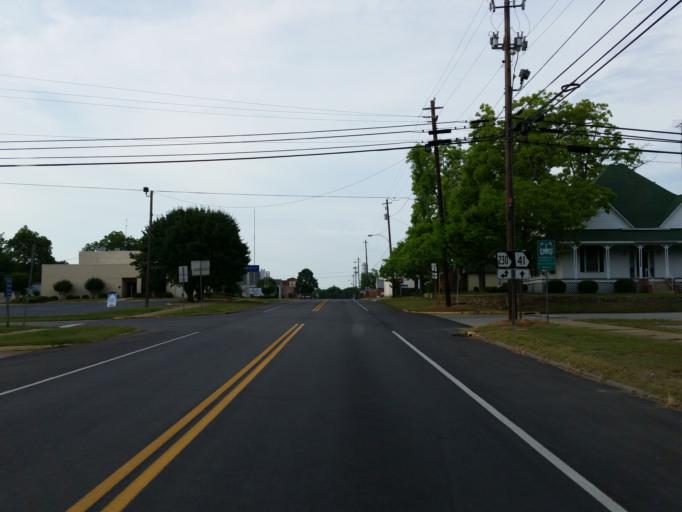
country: US
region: Georgia
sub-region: Dooly County
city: Unadilla
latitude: 32.2600
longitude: -83.7372
